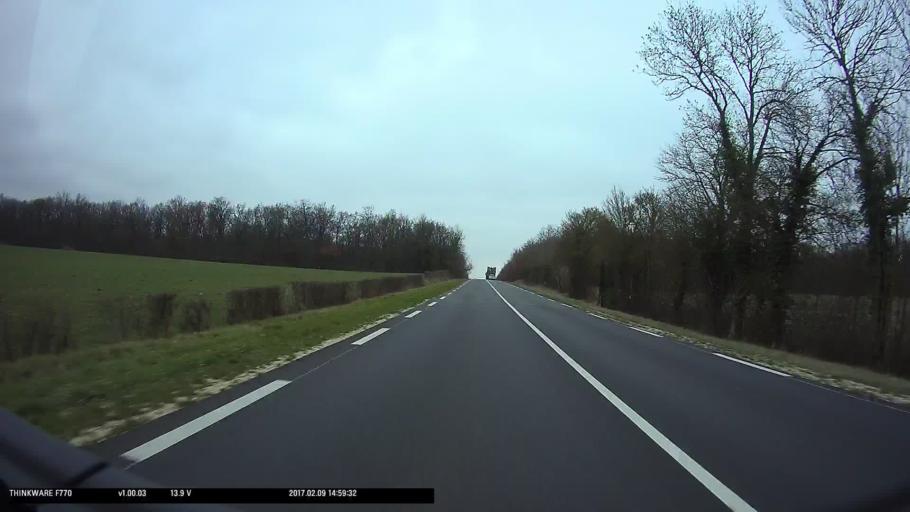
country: FR
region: Centre
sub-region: Departement du Cher
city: Levet
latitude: 46.8245
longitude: 2.4245
